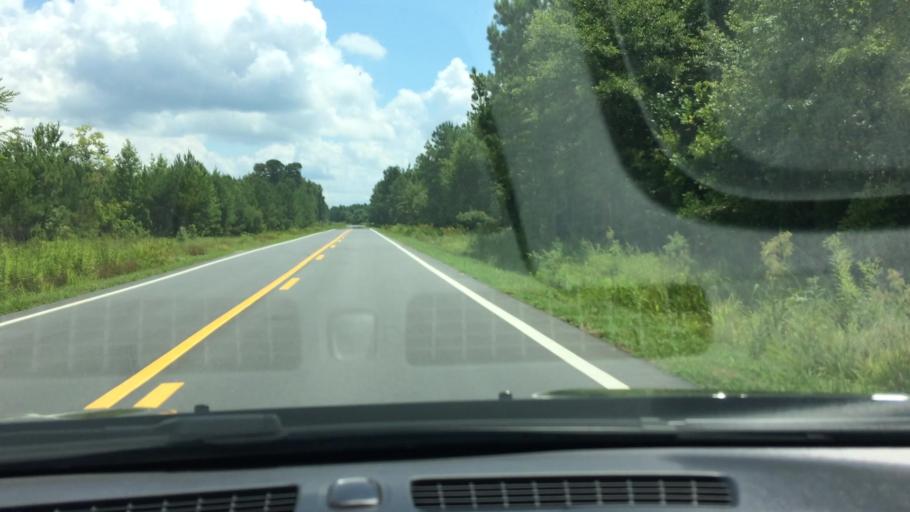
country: US
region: North Carolina
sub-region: Craven County
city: Vanceboro
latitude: 35.4288
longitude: -77.1855
